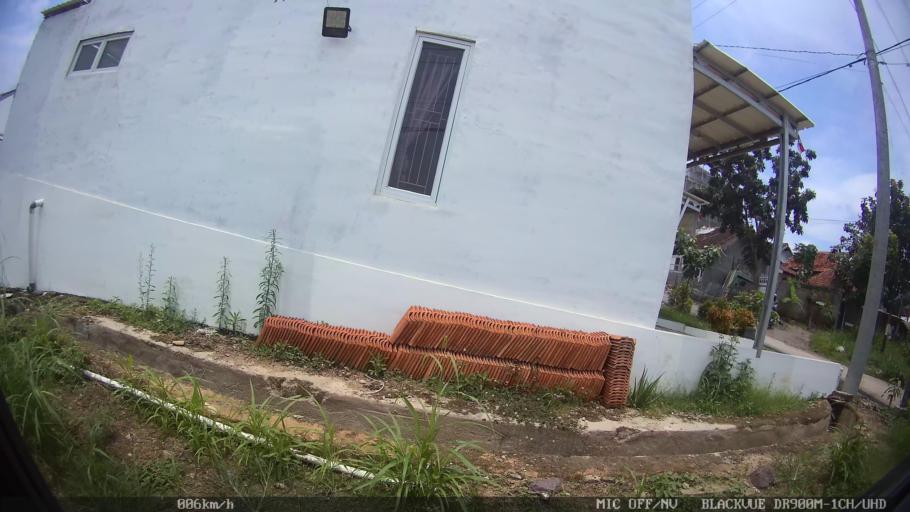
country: ID
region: Lampung
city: Bandarlampung
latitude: -5.4118
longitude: 105.1999
